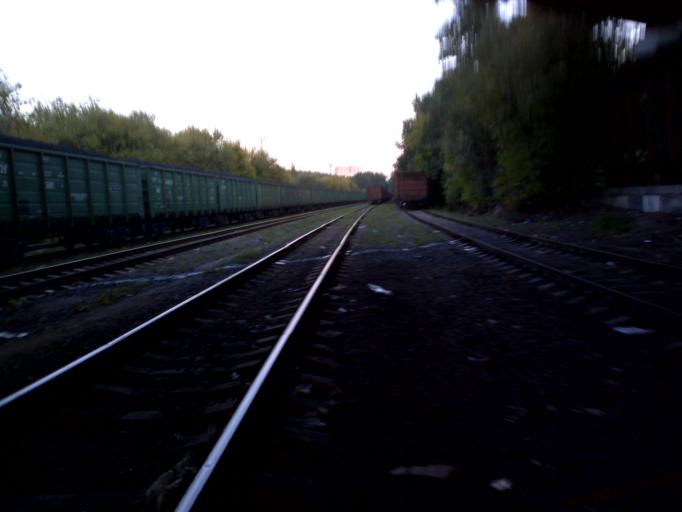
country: RU
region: Moscow
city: Biryulevo
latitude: 55.5889
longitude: 37.6751
